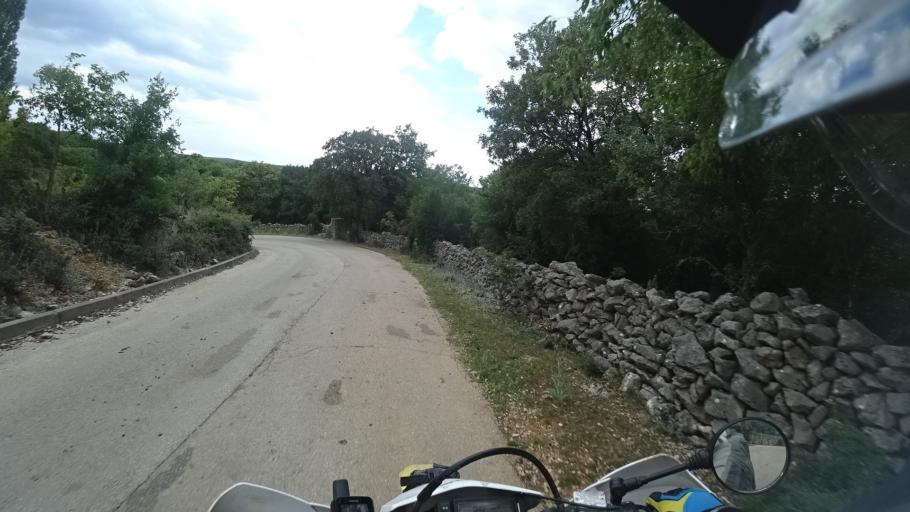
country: HR
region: Zadarska
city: Gracac
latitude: 44.1932
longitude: 15.9086
